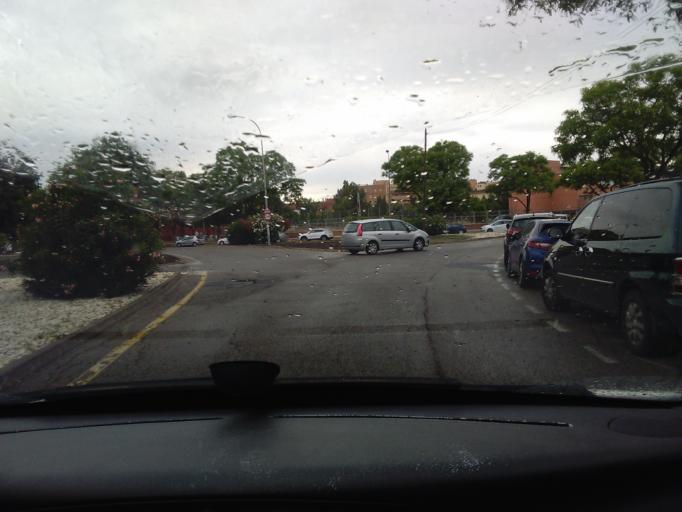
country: ES
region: Andalusia
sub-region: Provincia de Sevilla
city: Sevilla
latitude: 37.3999
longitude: -5.9375
